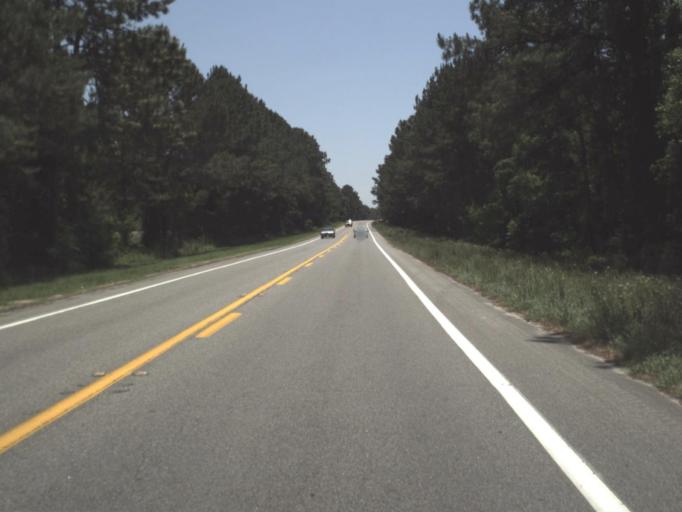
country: US
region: Florida
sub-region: Suwannee County
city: Live Oak
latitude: 30.3547
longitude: -83.1150
